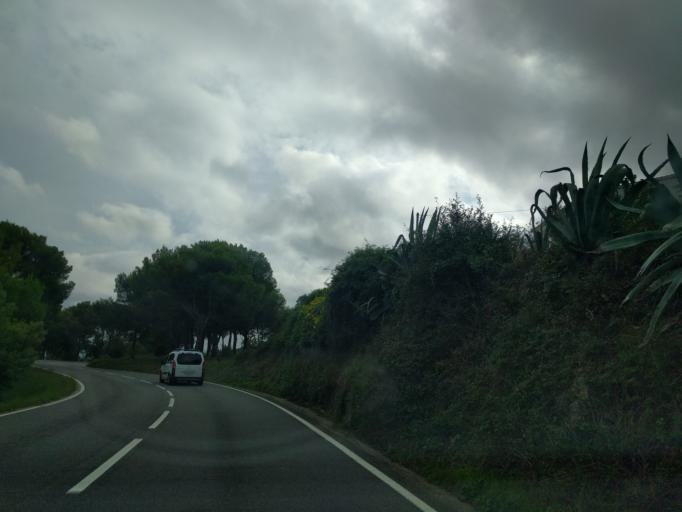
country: ES
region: Catalonia
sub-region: Provincia de Girona
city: Llanca
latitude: 42.3559
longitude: 3.1684
